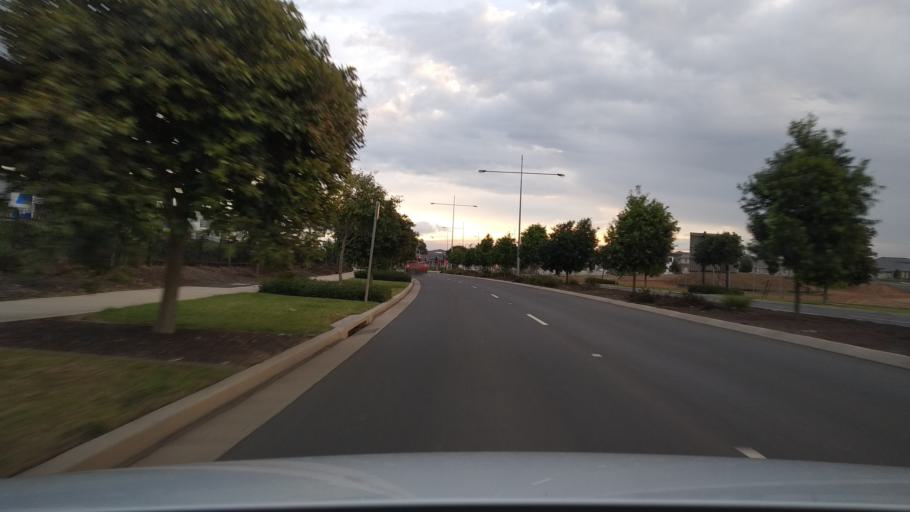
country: AU
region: New South Wales
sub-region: Camden
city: Narellan
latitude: -34.0012
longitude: 150.7370
